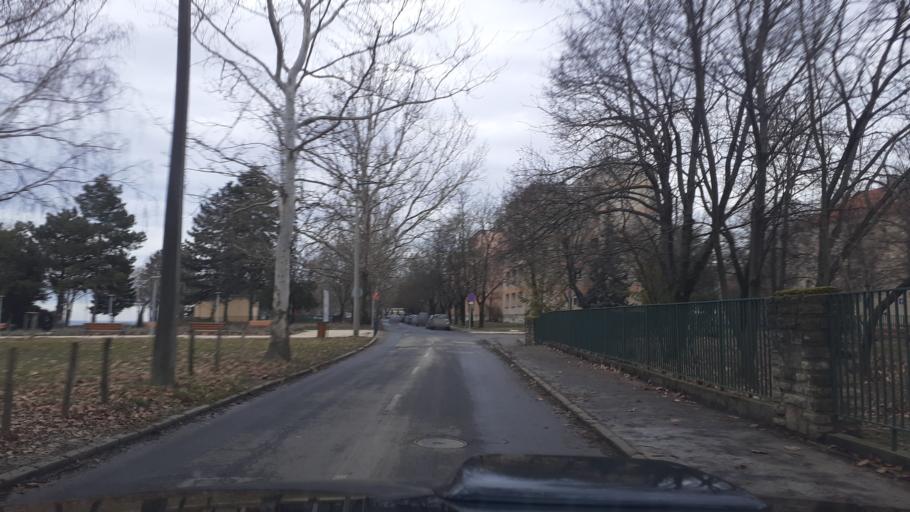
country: HU
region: Fejer
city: Dunaujvaros
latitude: 46.9646
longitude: 18.9448
